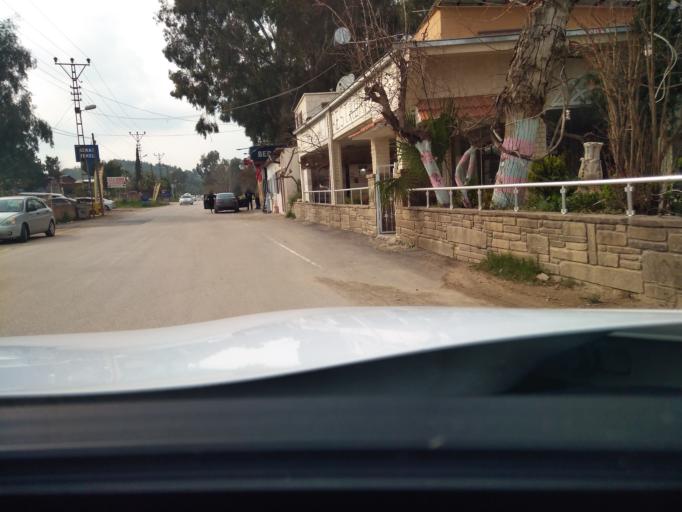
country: TR
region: Adana
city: Adana
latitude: 37.0648
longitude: 35.2852
